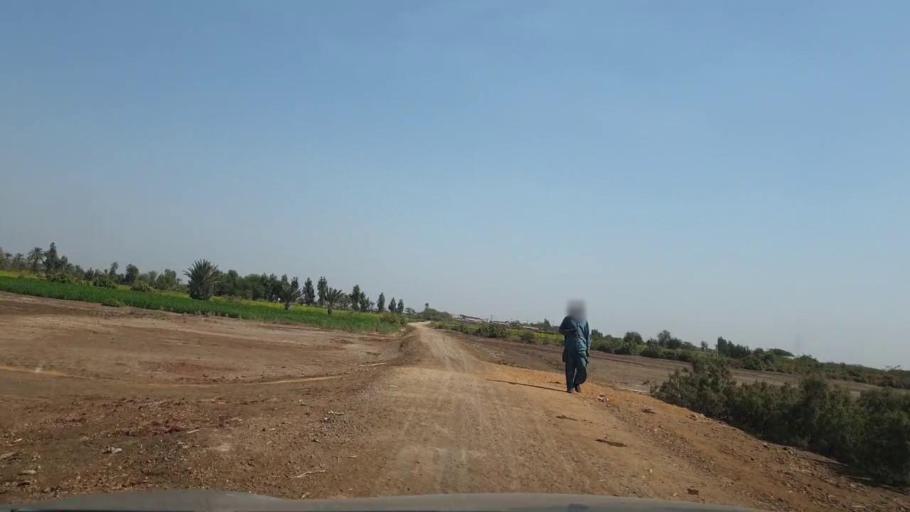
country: PK
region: Sindh
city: Berani
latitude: 25.6310
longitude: 68.8712
